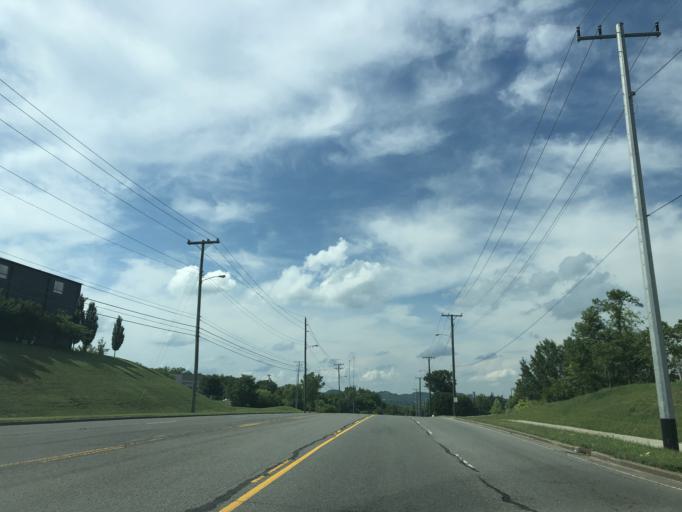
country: US
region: Tennessee
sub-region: Davidson County
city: Nashville
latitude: 36.2186
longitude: -86.7820
